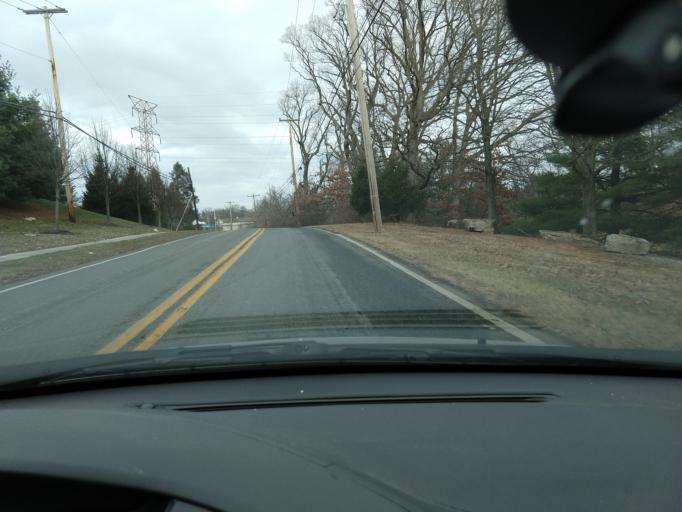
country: US
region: Pennsylvania
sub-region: Chester County
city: South Pottstown
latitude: 40.2245
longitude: -75.6564
